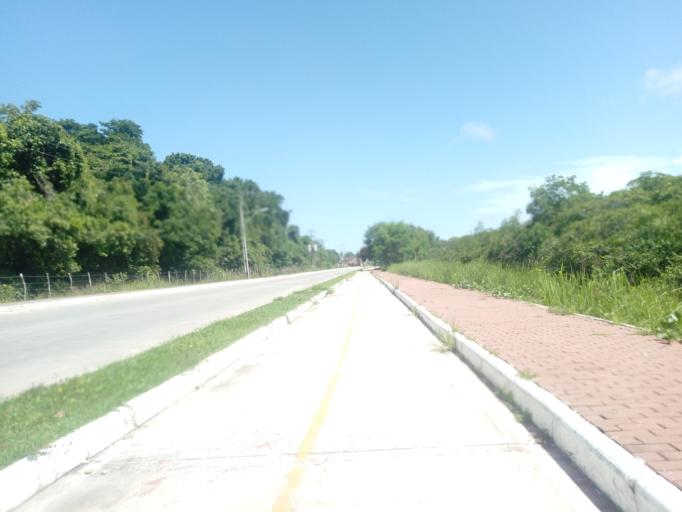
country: BR
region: Pernambuco
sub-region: Sirinhaem
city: Sirinhaem
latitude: -8.5225
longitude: -35.0104
